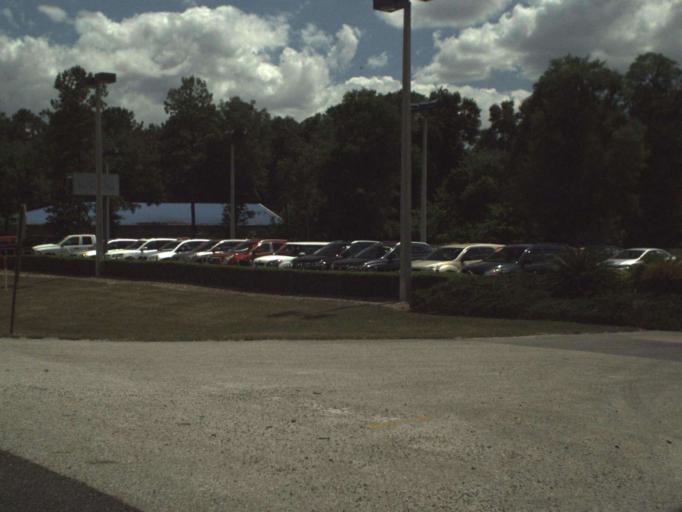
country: US
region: Florida
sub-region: Marion County
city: Ocala
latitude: 29.2300
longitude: -82.1497
